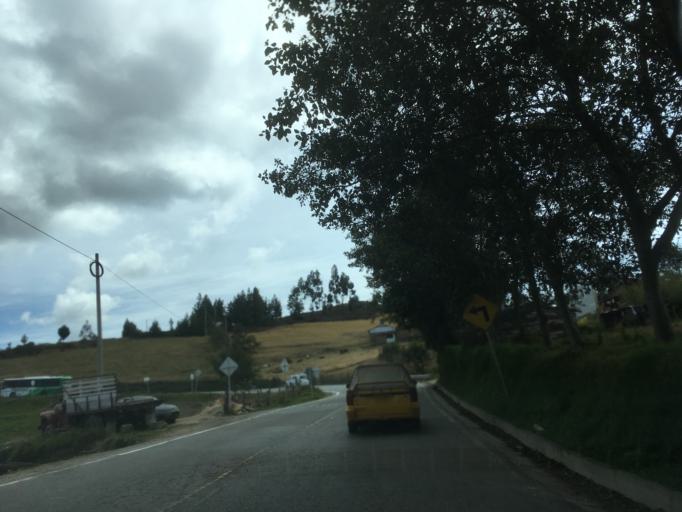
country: CO
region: Boyaca
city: Sogamoso
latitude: 5.6391
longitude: -72.9203
